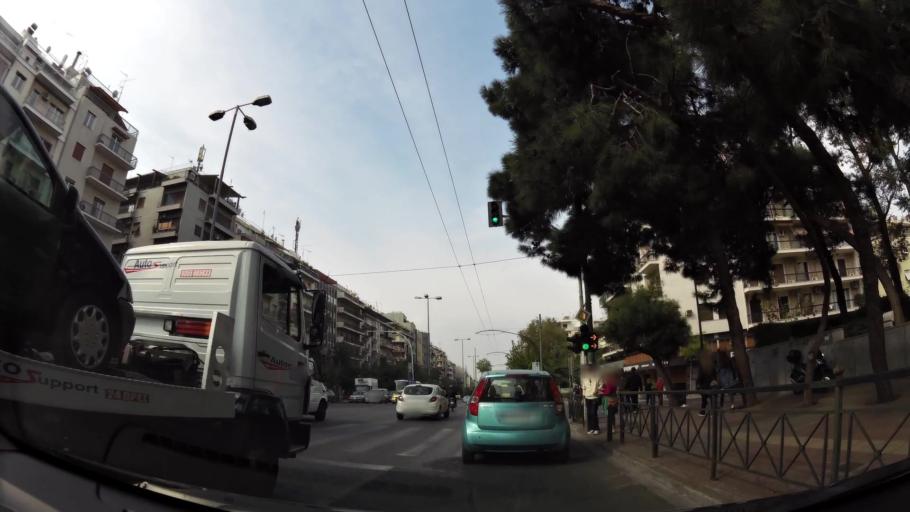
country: GR
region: Attica
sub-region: Nomarchia Athinas
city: Kipseli
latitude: 37.9884
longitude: 23.7520
